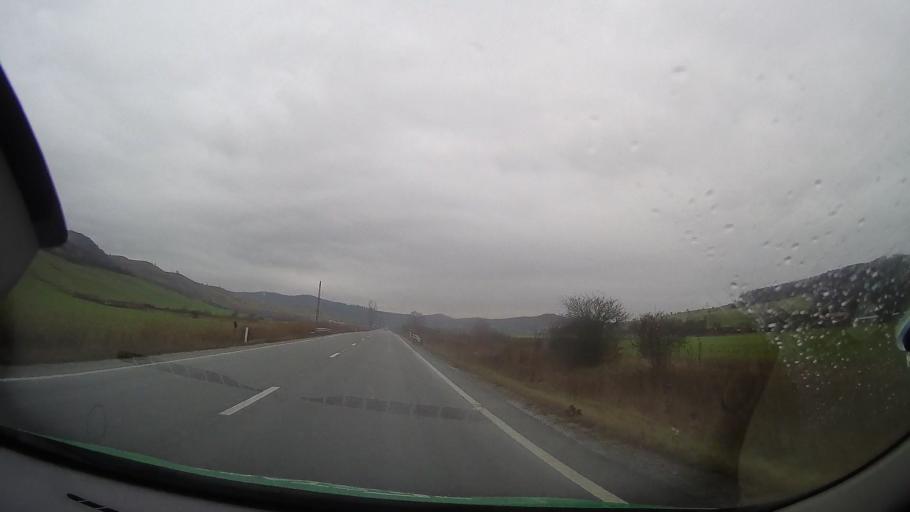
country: RO
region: Bistrita-Nasaud
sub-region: Comuna Teaca
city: Teaca
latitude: 46.9306
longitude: 24.4820
